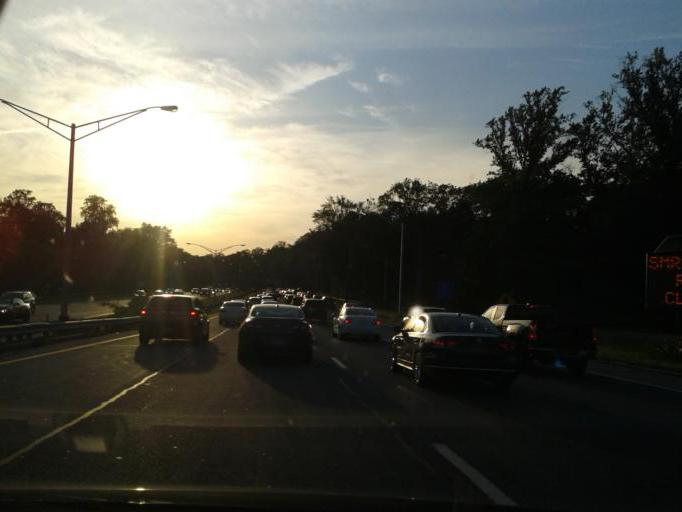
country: US
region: New York
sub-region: Westchester County
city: Bronxville
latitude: 40.9239
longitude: -73.8248
